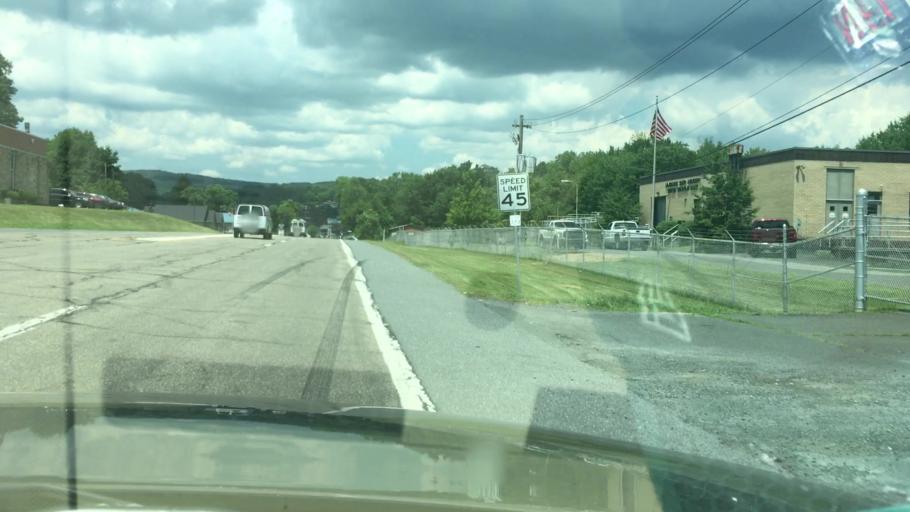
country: US
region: Pennsylvania
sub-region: Schuylkill County
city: Minersville
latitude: 40.6843
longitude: -76.2551
